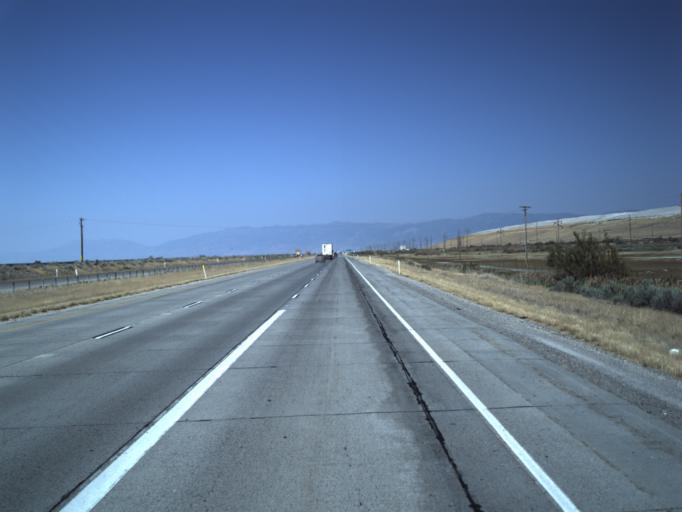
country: US
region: Utah
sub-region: Salt Lake County
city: Magna
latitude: 40.7493
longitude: -112.1779
